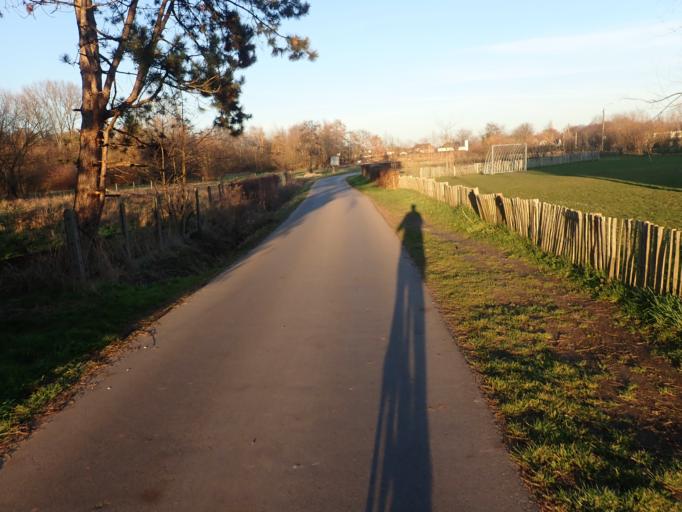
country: BE
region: Flanders
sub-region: Provincie Antwerpen
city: Sint-Amands
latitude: 51.0662
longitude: 4.1952
